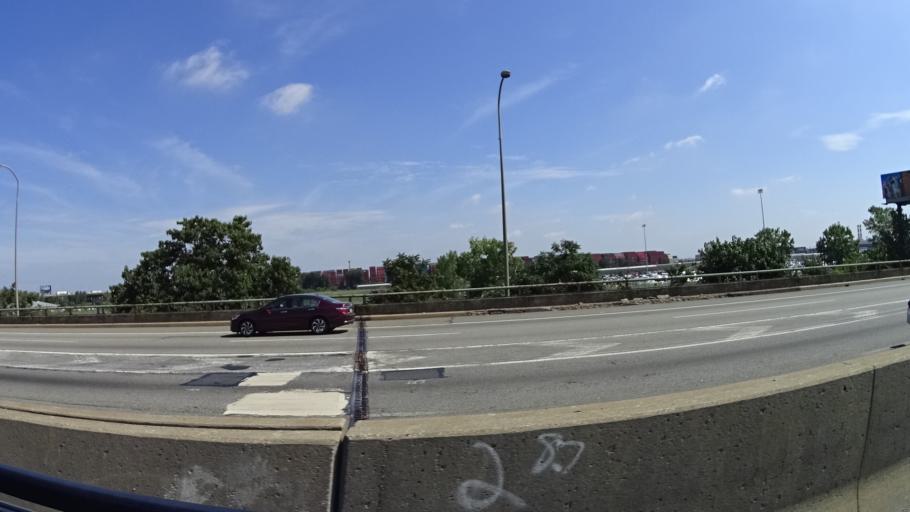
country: US
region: New Jersey
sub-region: Essex County
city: Newark
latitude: 40.7043
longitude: -74.1459
